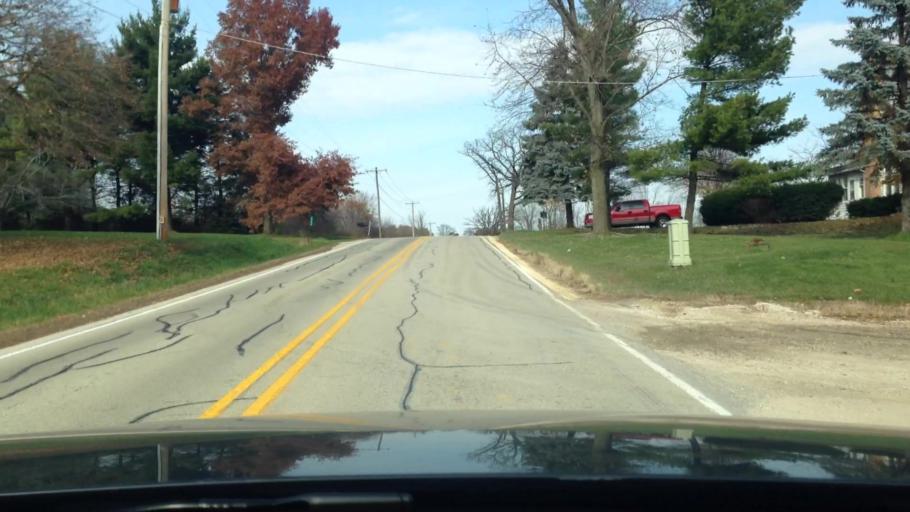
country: US
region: Illinois
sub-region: McHenry County
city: Woodstock
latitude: 42.2629
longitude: -88.4507
